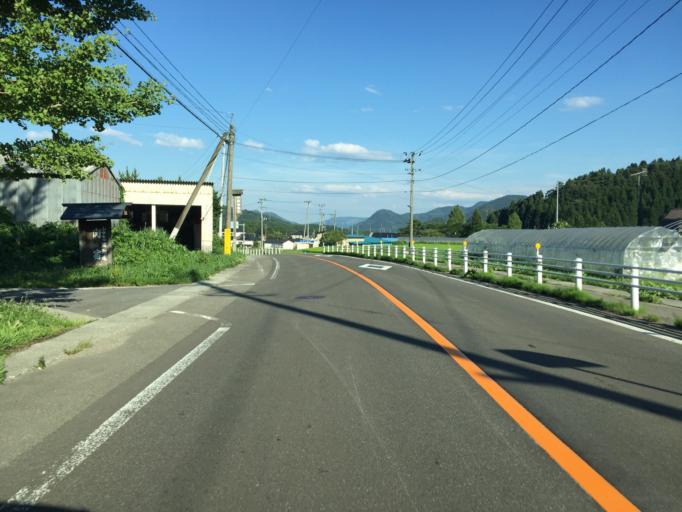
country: JP
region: Miyagi
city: Shiroishi
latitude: 37.9973
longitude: 140.4368
